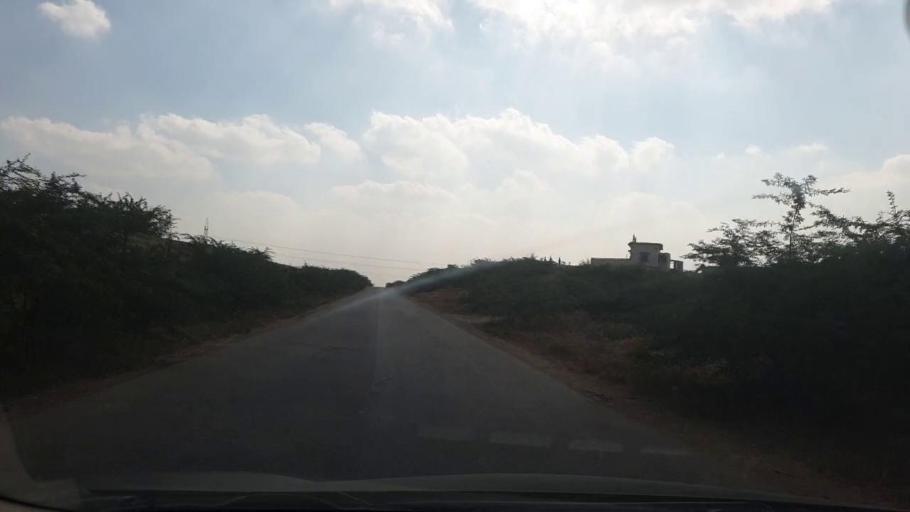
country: PK
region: Sindh
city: Malir Cantonment
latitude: 25.0137
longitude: 67.3527
